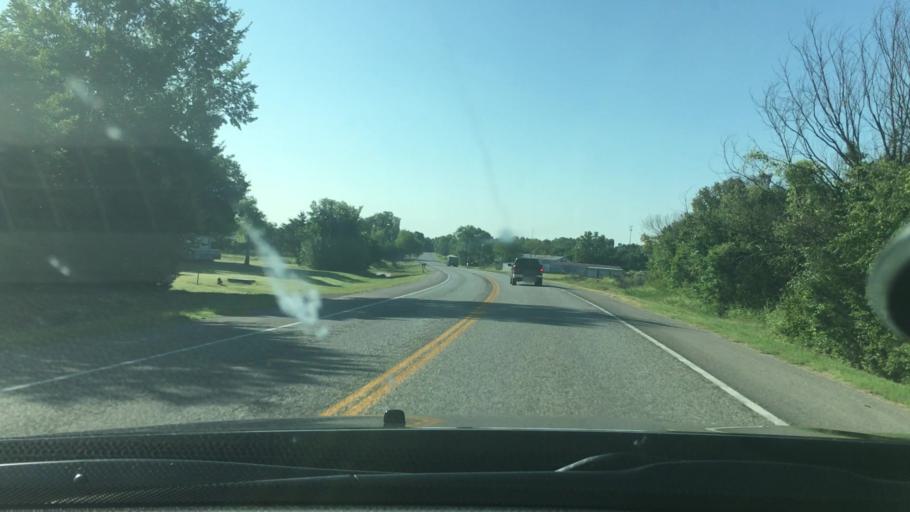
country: US
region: Oklahoma
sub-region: Johnston County
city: Tishomingo
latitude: 34.2489
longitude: -96.7585
